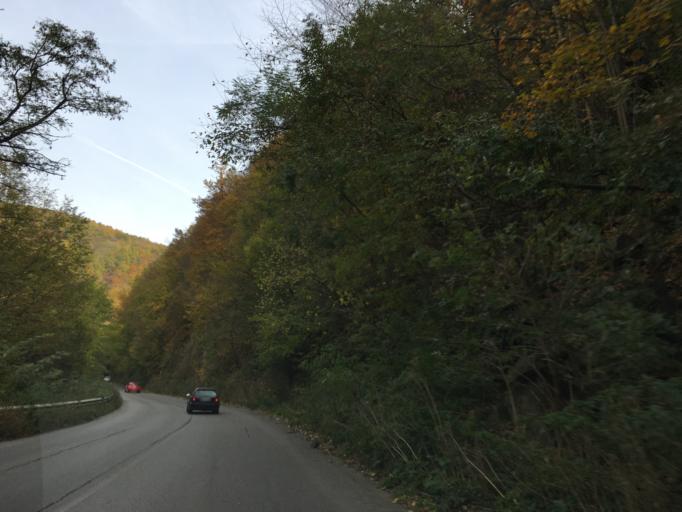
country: BG
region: Sofia-Capital
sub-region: Stolichna Obshtina
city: Sofia
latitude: 42.5527
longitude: 23.4368
